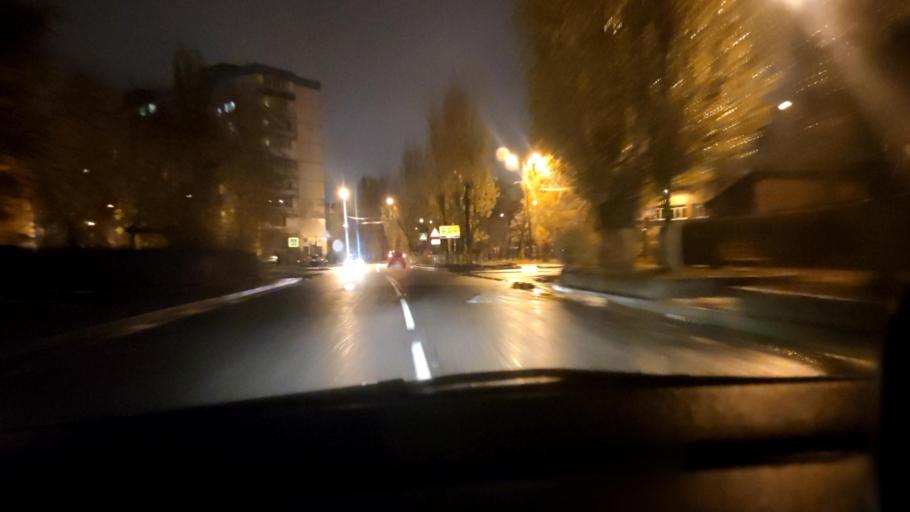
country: RU
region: Voronezj
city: Voronezh
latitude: 51.6503
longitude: 39.1434
